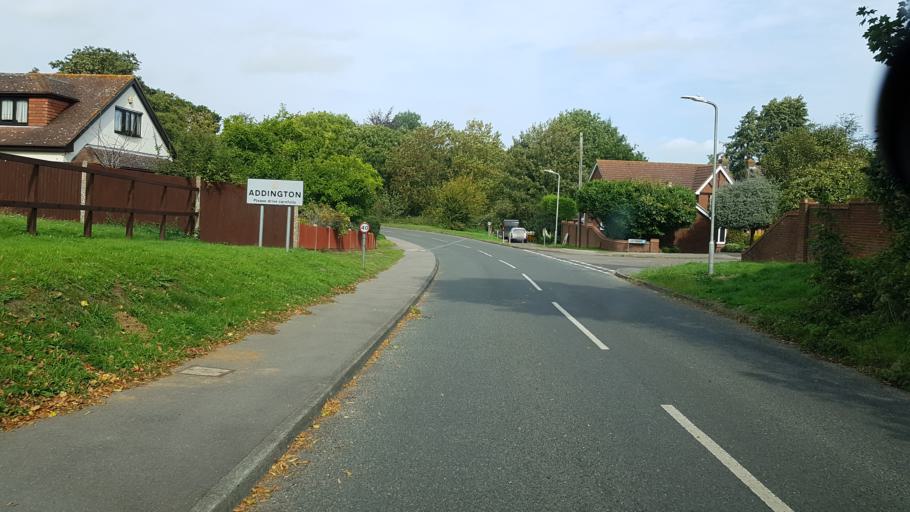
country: GB
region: England
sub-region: Kent
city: West Malling
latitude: 51.3031
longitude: 0.3810
